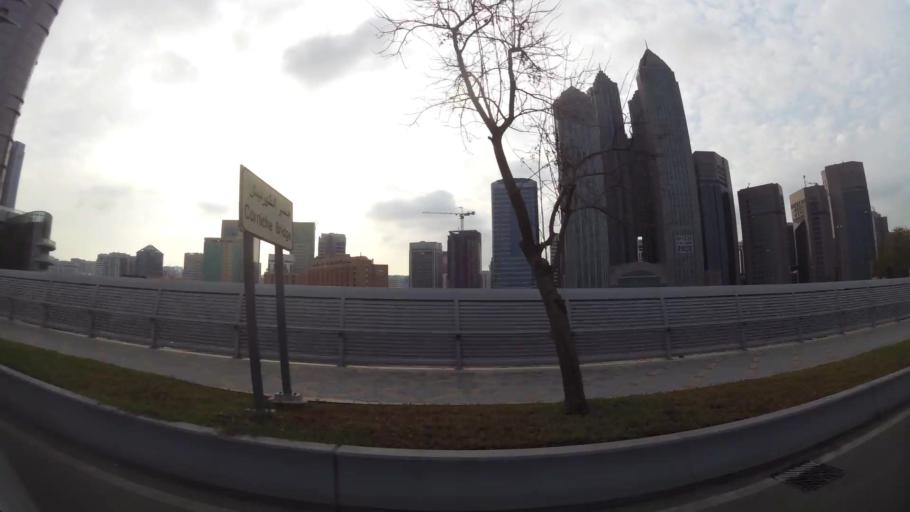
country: AE
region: Abu Dhabi
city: Abu Dhabi
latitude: 24.5015
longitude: 54.3656
